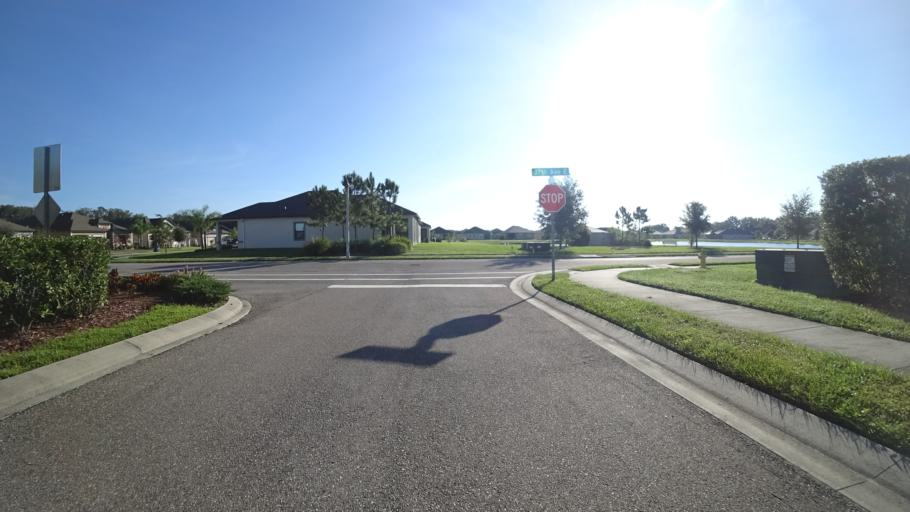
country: US
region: Florida
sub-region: Manatee County
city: Memphis
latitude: 27.5822
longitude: -82.5268
